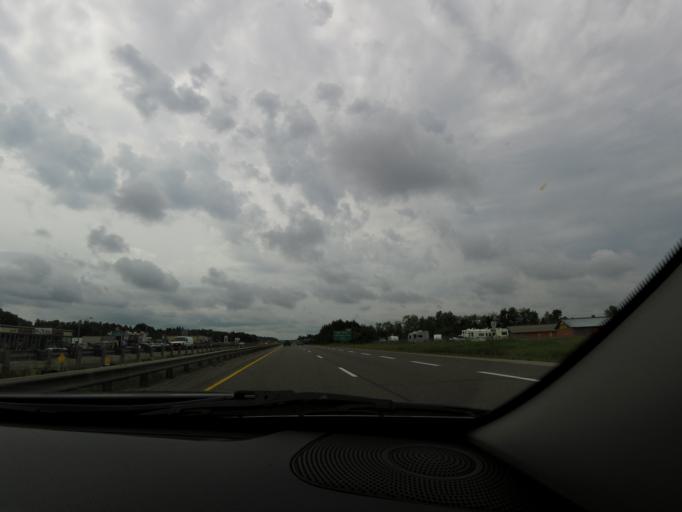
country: CA
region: Ontario
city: Orillia
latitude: 44.6388
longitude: -79.4259
